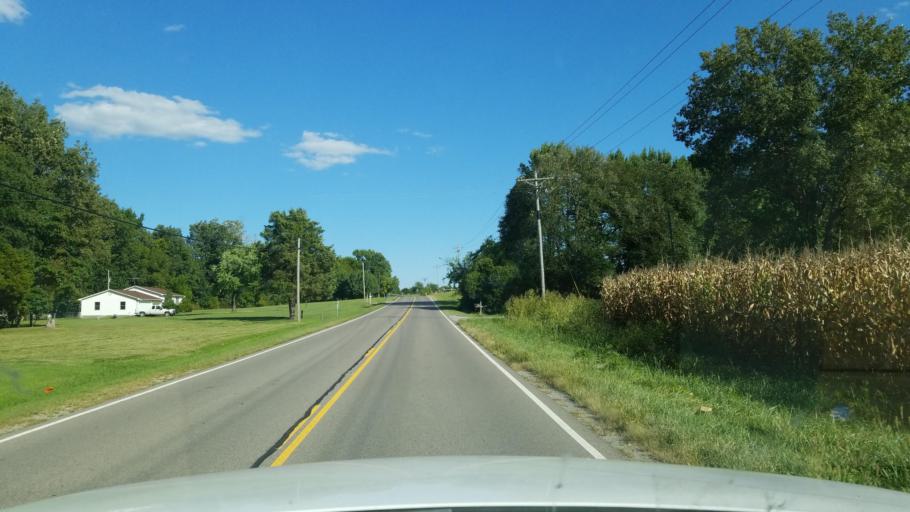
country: US
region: Illinois
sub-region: Saline County
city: Harrisburg
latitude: 37.6388
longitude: -88.5261
